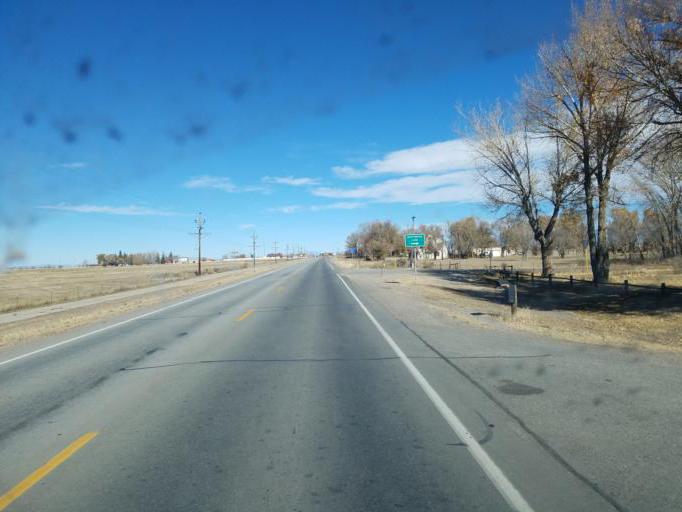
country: US
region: Colorado
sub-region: Alamosa County
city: Alamosa East
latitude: 37.4833
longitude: -105.8573
